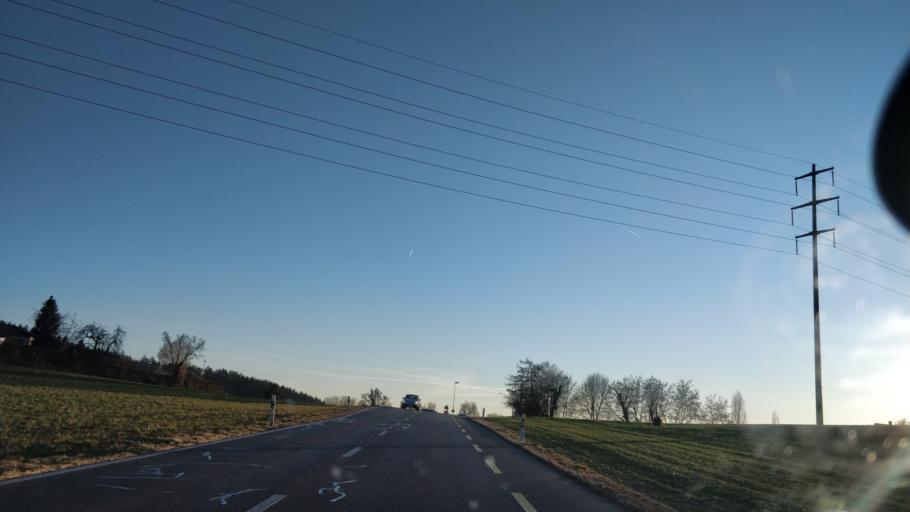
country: CH
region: Zurich
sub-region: Bezirk Buelach
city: Rorbas
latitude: 47.5207
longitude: 8.5690
